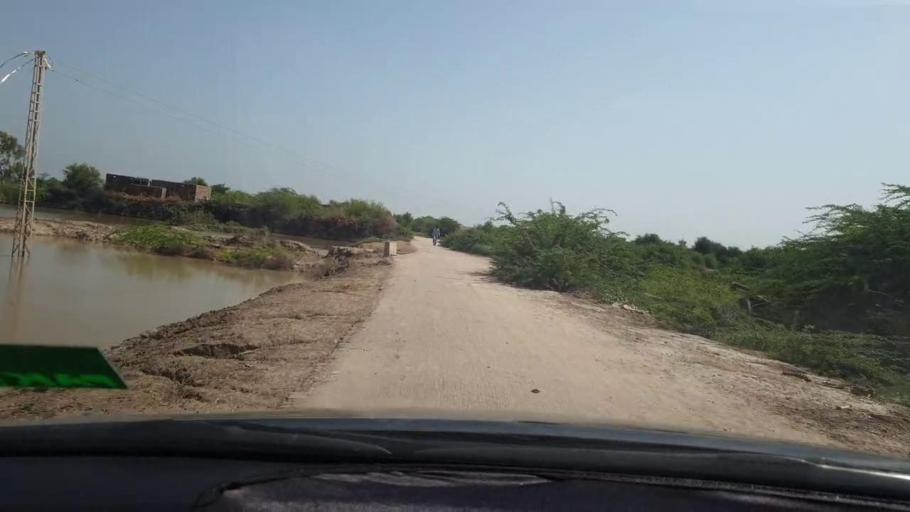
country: PK
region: Sindh
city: Digri
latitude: 24.9417
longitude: 69.1866
